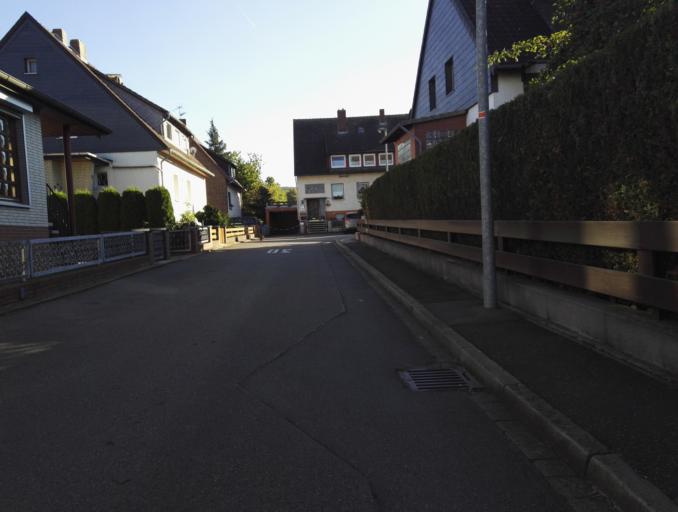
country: DE
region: Lower Saxony
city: Schellerten
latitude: 52.1327
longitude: 10.0705
